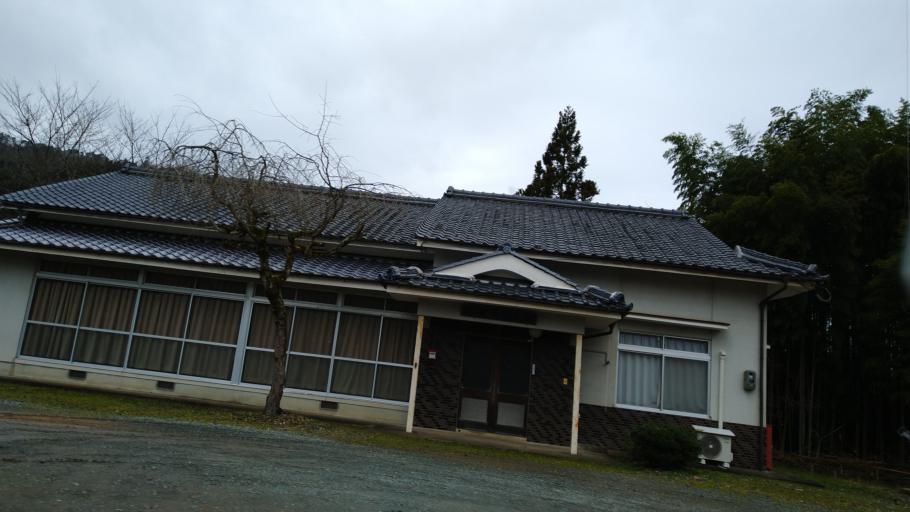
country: JP
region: Kyoto
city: Ayabe
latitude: 35.3264
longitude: 135.3550
